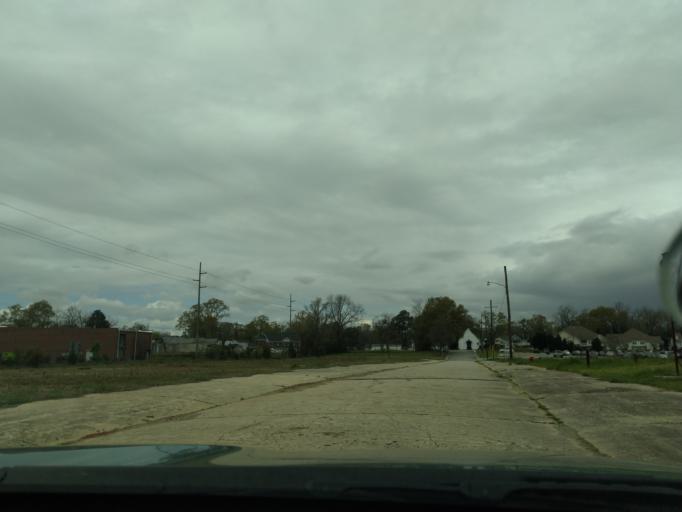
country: US
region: North Carolina
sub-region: Pitt County
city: Greenville
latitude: 35.6091
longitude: -77.3790
